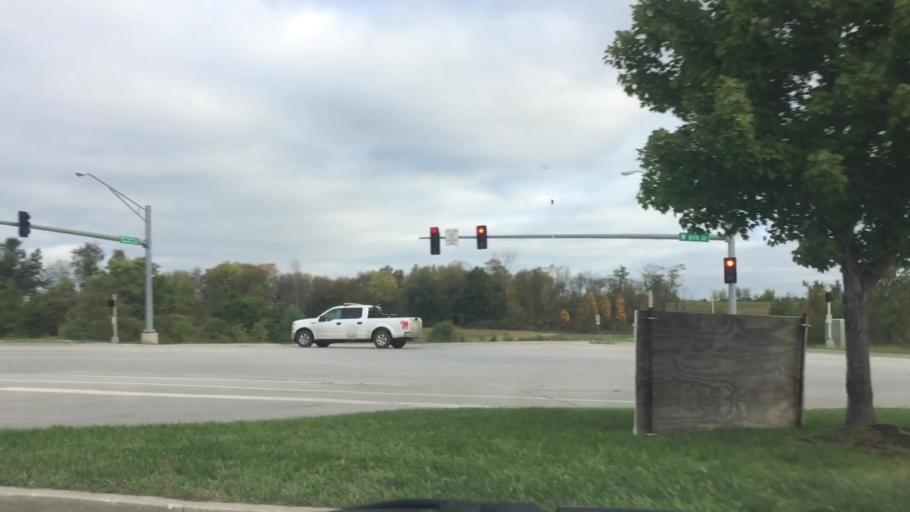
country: US
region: Missouri
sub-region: Clay County
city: Kearney
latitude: 39.3676
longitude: -94.3762
